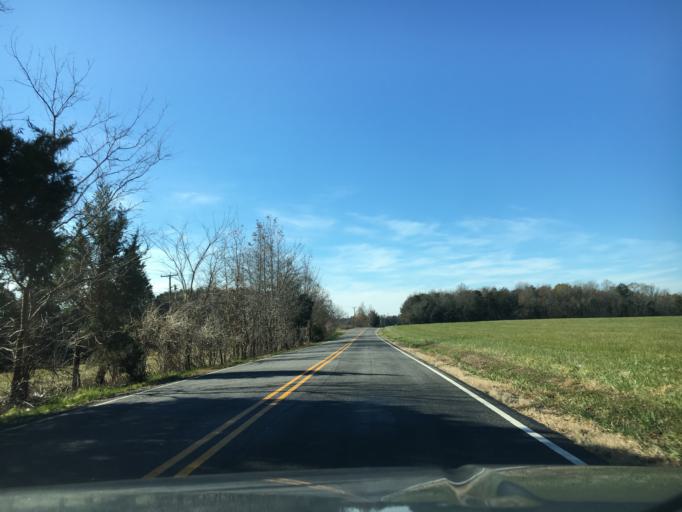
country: US
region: Virginia
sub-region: Cumberland County
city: Cumberland
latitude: 37.4602
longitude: -78.2872
